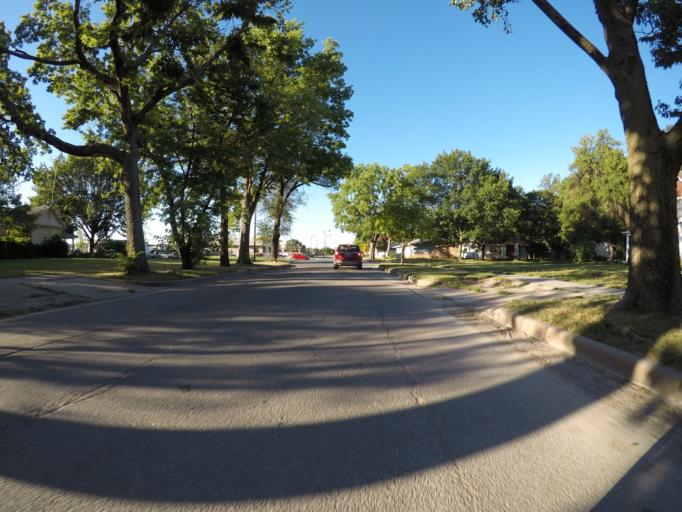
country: US
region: Kansas
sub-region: Riley County
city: Manhattan
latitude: 39.1882
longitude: -96.5617
